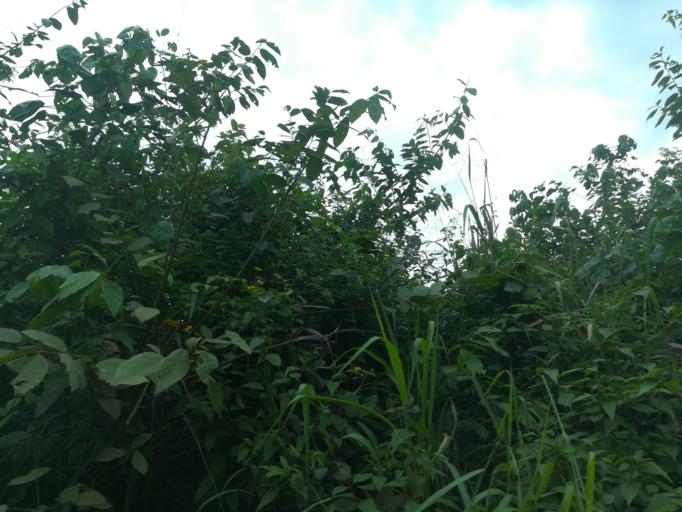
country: NG
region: Ogun
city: Odogbolu
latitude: 6.6608
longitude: 3.7111
